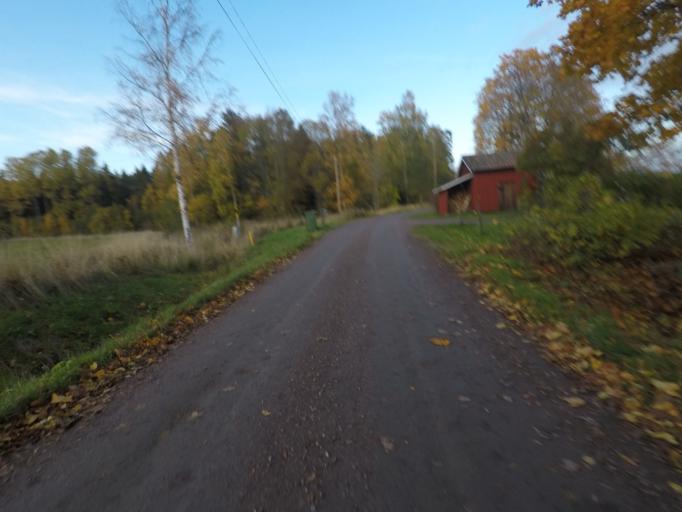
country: SE
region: OErebro
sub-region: Karlskoga Kommun
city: Karlskoga
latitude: 59.2973
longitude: 14.5085
